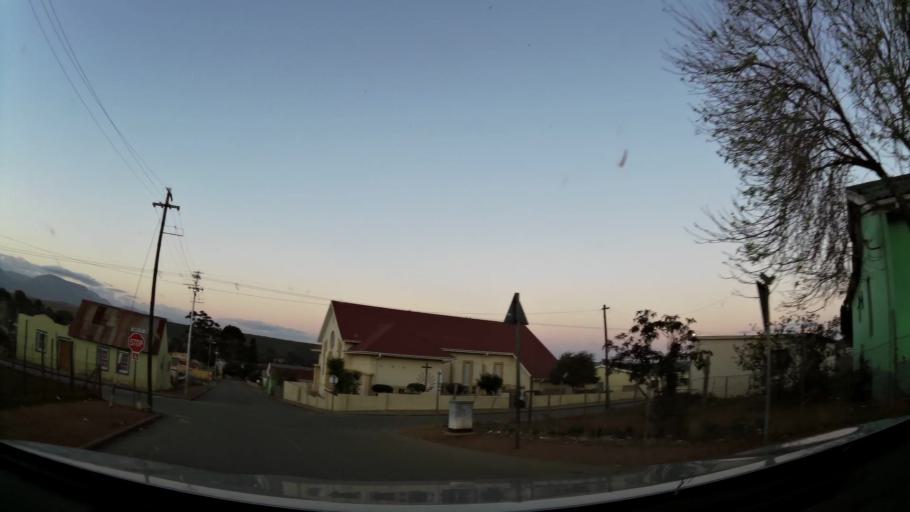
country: ZA
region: Western Cape
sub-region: Eden District Municipality
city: Riversdale
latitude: -34.0976
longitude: 21.2626
